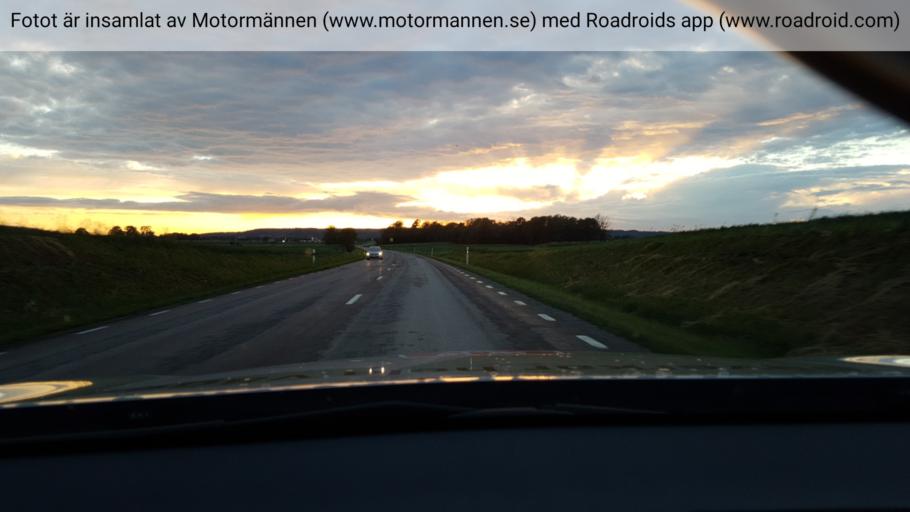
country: SE
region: Vaestra Goetaland
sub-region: Falkopings Kommun
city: Falkoeping
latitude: 58.1519
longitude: 13.6012
